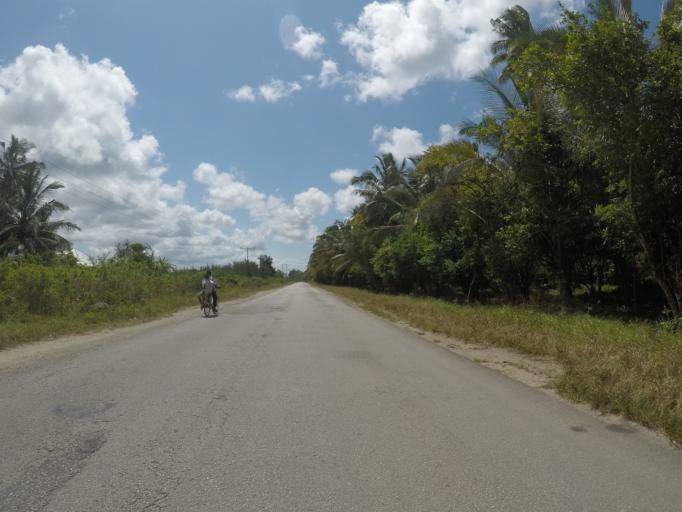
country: TZ
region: Zanzibar Central/South
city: Nganane
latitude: -6.2749
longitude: 39.4305
